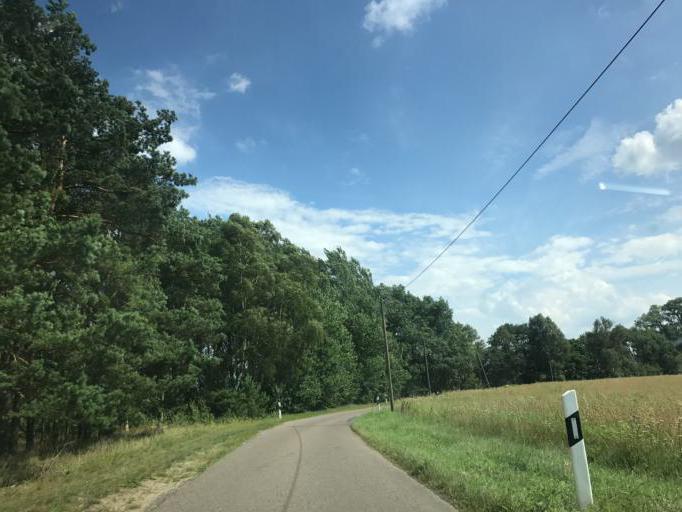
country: DE
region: Mecklenburg-Vorpommern
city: Wesenberg
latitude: 53.3167
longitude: 12.8681
